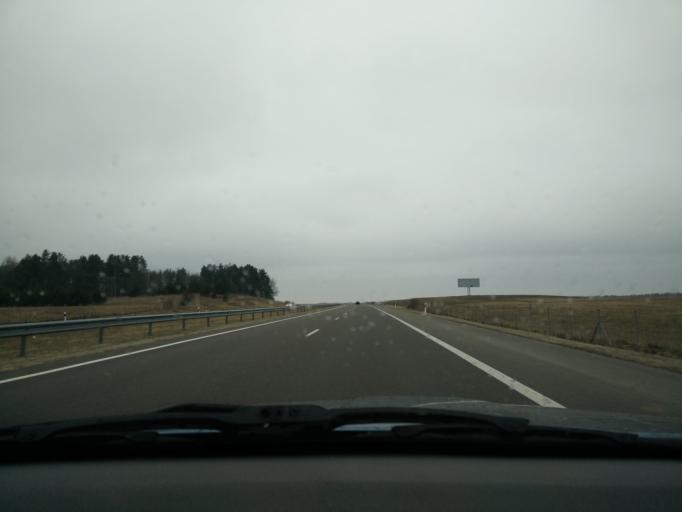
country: LT
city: Silale
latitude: 55.5966
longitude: 22.1242
